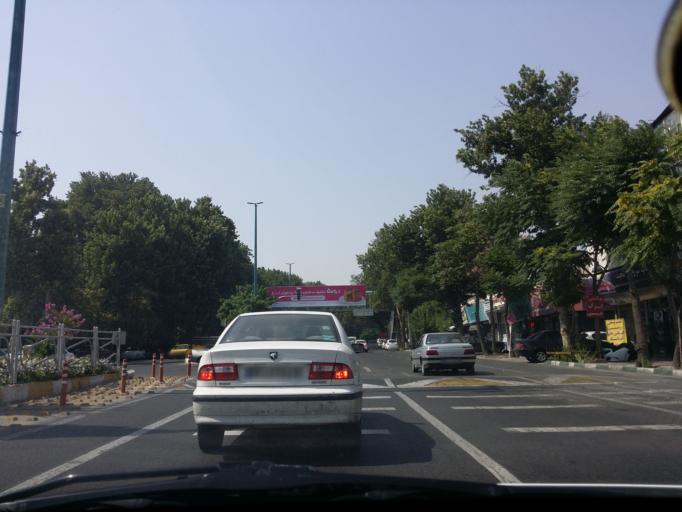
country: IR
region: Alborz
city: Karaj
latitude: 35.8012
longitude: 51.0012
